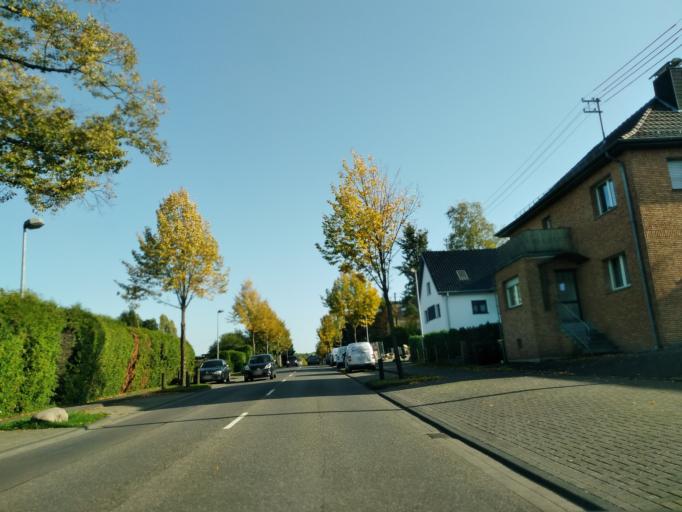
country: DE
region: North Rhine-Westphalia
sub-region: Regierungsbezirk Koln
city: Hennef
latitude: 50.7412
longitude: 7.3540
